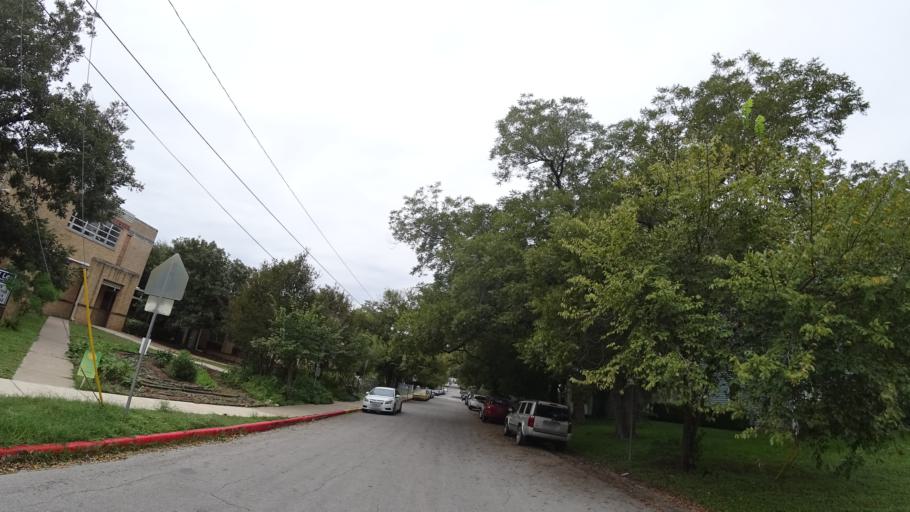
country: US
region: Texas
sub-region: Travis County
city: Austin
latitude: 30.2938
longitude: -97.7268
